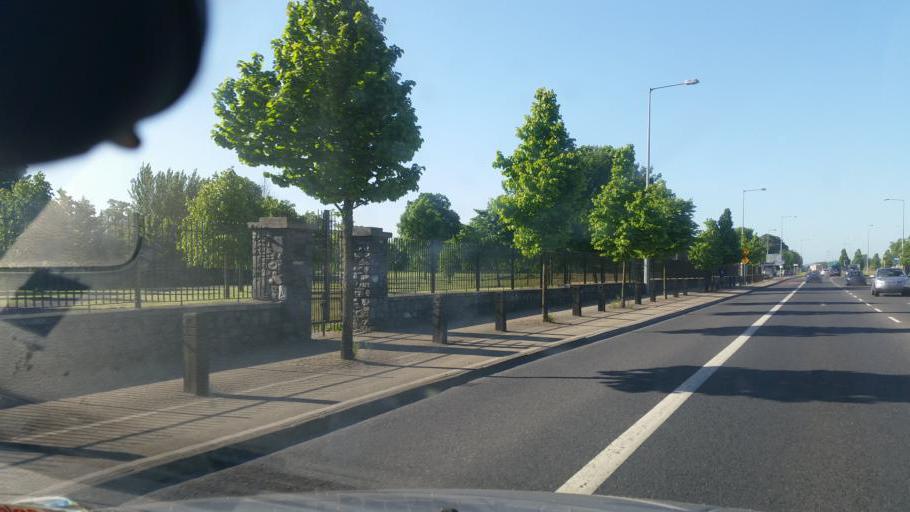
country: IE
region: Leinster
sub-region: Fingal County
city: Blanchardstown
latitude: 53.3878
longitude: -6.4013
